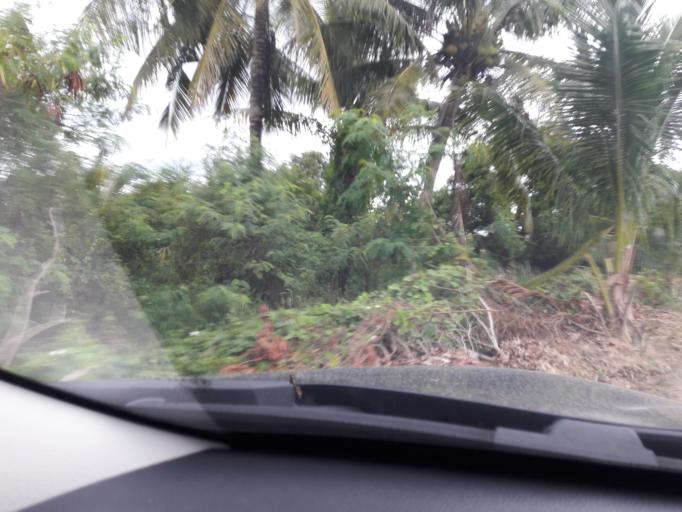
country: TH
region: Ratchaburi
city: Bang Phae
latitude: 13.6229
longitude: 99.9404
